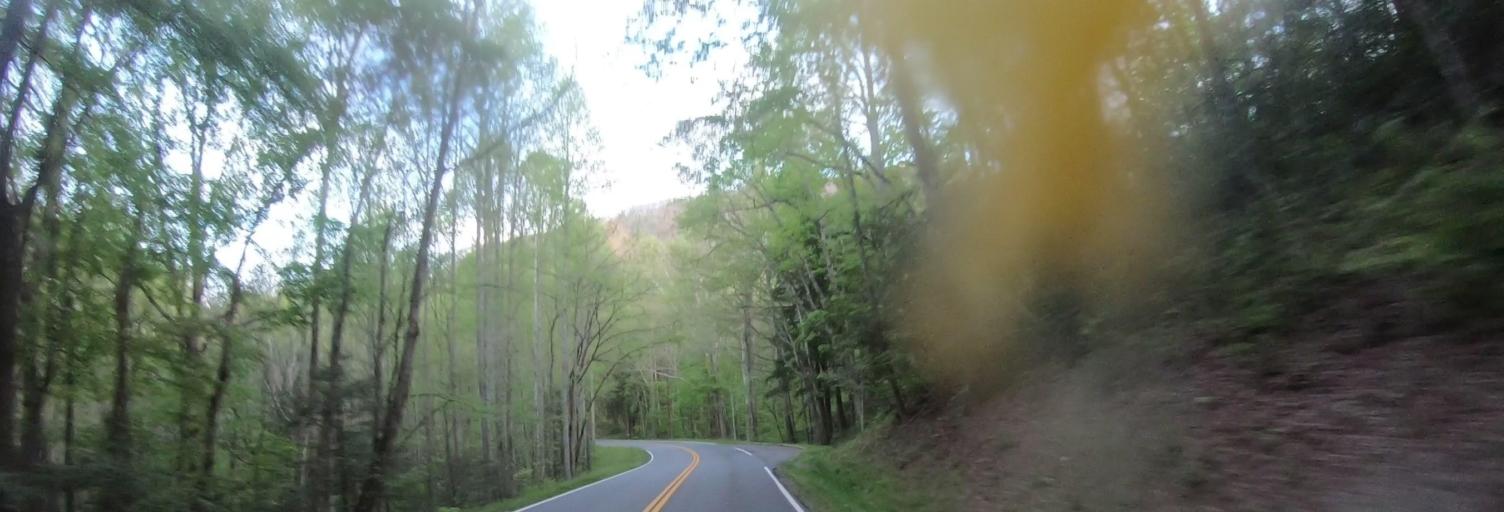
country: US
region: Tennessee
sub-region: Sevier County
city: Gatlinburg
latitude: 35.6662
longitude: -83.5264
